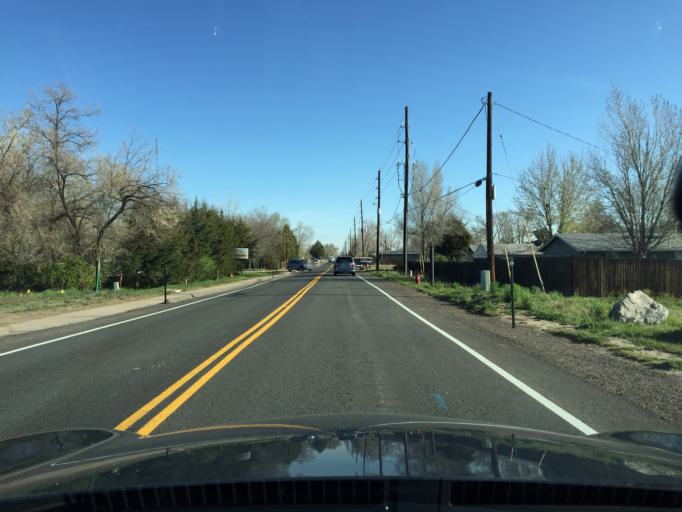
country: US
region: Colorado
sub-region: Boulder County
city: Erie
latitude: 40.0467
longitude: -105.0555
